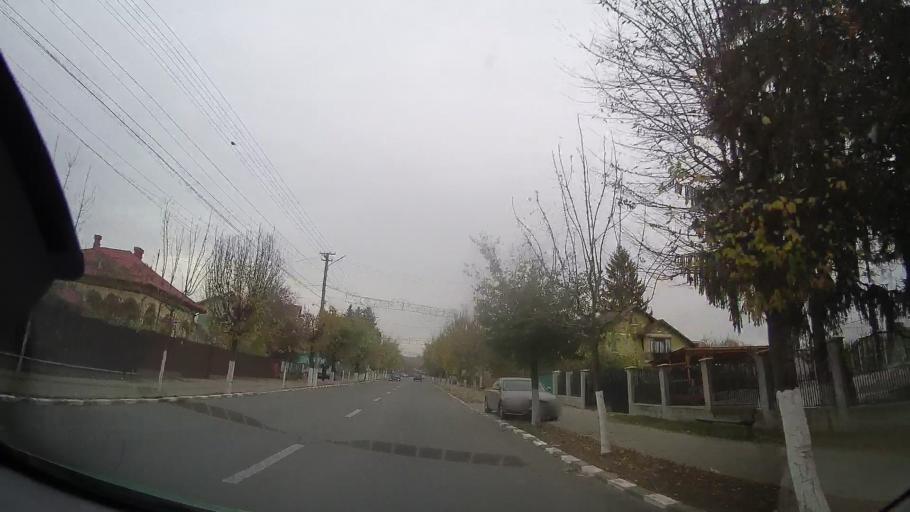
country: RO
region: Prahova
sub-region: Oras Urlati
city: Urlati
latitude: 44.9870
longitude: 26.2339
